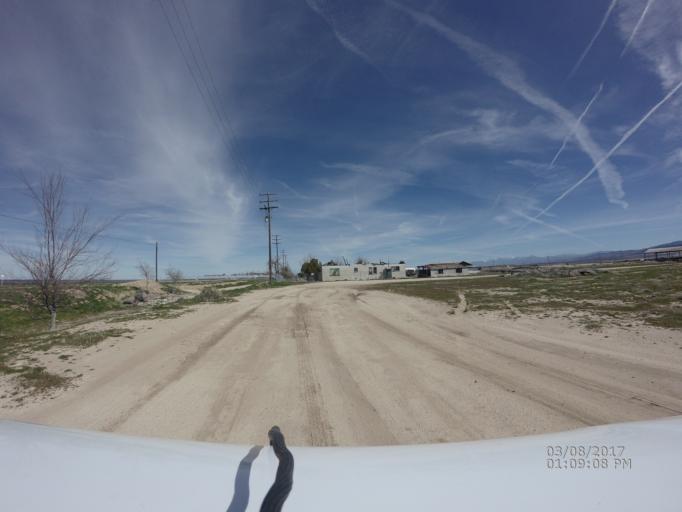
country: US
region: California
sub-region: Los Angeles County
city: Leona Valley
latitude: 34.7183
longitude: -118.2987
